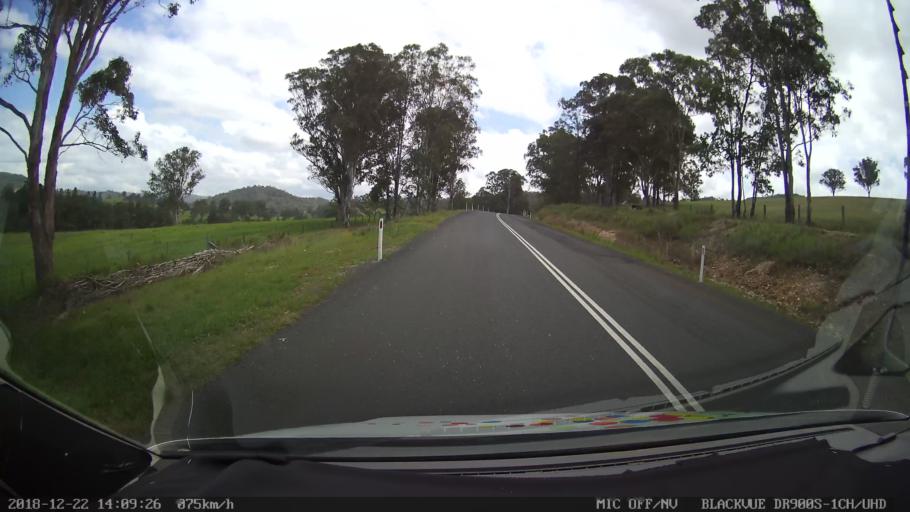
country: AU
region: New South Wales
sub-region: Clarence Valley
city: Coutts Crossing
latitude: -29.9864
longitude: 152.7173
